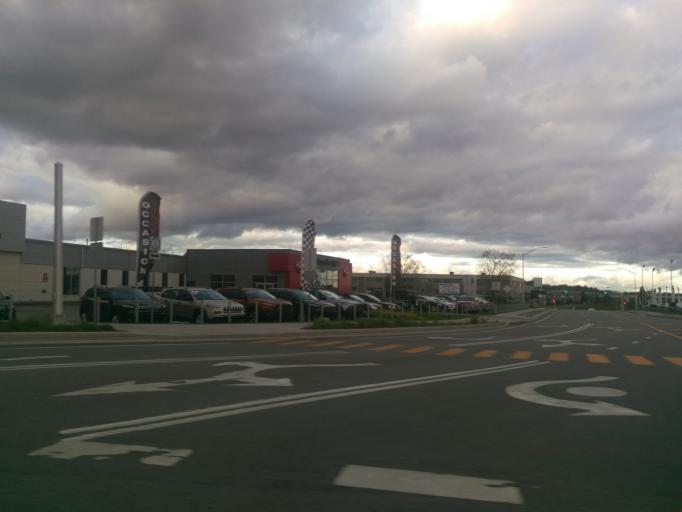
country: CA
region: Quebec
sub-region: Outaouais
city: Gatineau
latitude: 45.4671
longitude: -75.7380
